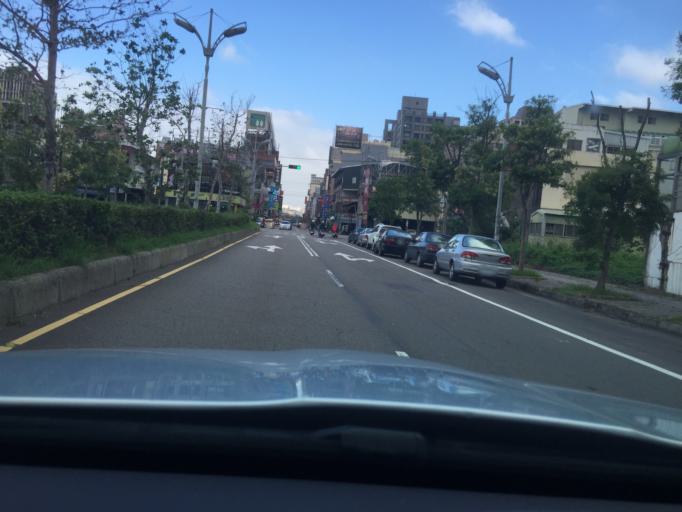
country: TW
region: Taiwan
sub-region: Hsinchu
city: Zhubei
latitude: 24.8238
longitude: 121.0079
